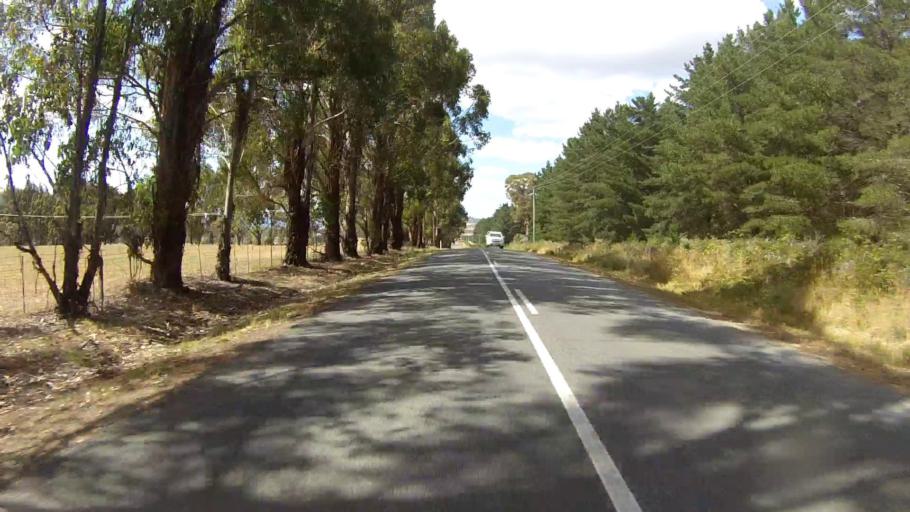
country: AU
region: Tasmania
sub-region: Derwent Valley
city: New Norfolk
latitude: -42.6777
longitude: 146.8024
